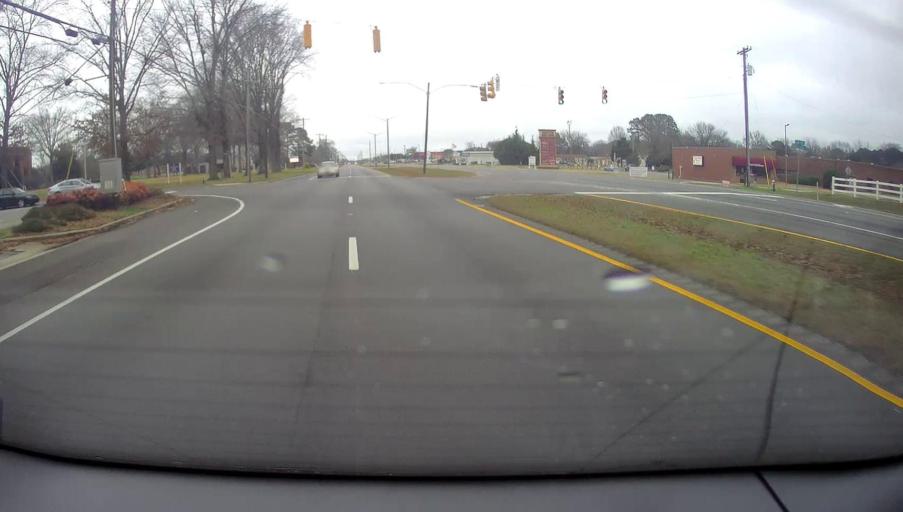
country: US
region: Alabama
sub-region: Morgan County
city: Flint City
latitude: 34.5521
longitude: -86.9736
